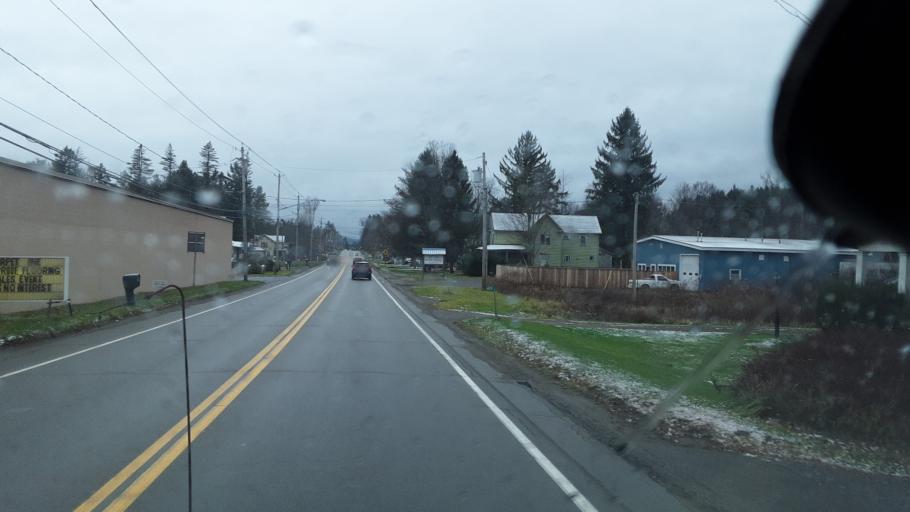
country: US
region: New York
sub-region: Cattaraugus County
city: Westons Mills
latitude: 42.0644
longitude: -78.3808
